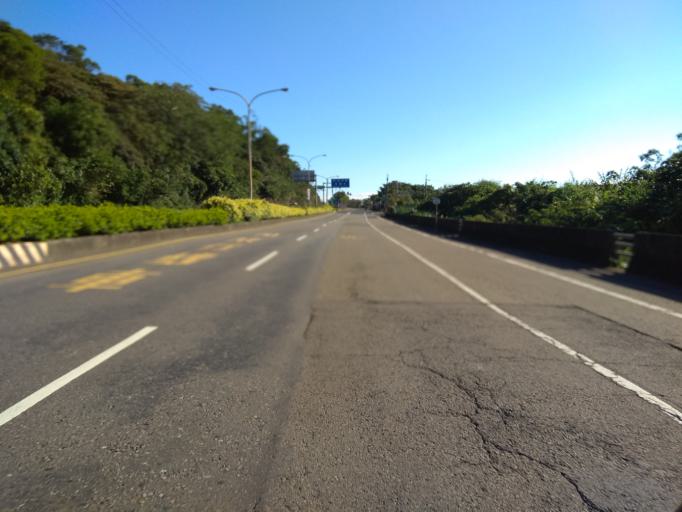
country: TW
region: Taiwan
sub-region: Hsinchu
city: Zhubei
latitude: 24.8950
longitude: 121.1084
